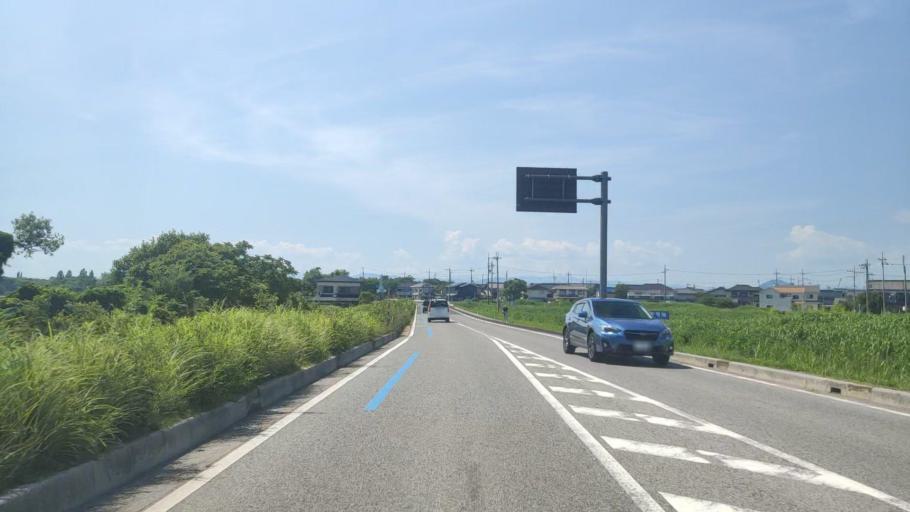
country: JP
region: Shiga Prefecture
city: Nagahama
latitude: 35.3858
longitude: 136.2465
